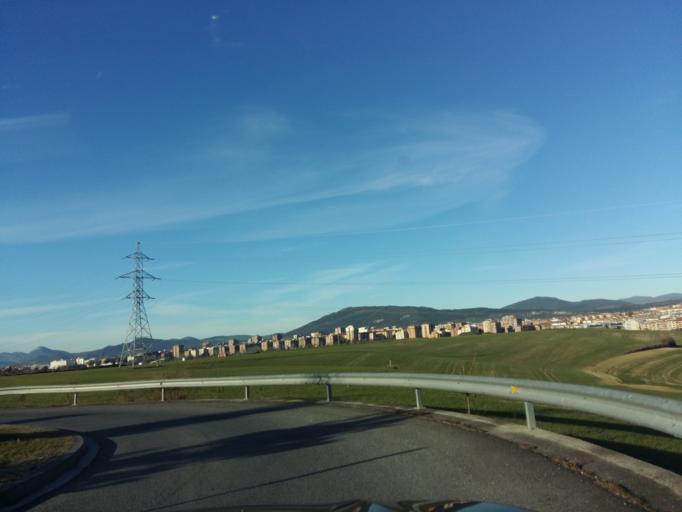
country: ES
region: Navarre
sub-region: Provincia de Navarra
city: Iturrama
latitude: 42.7893
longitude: -1.6460
